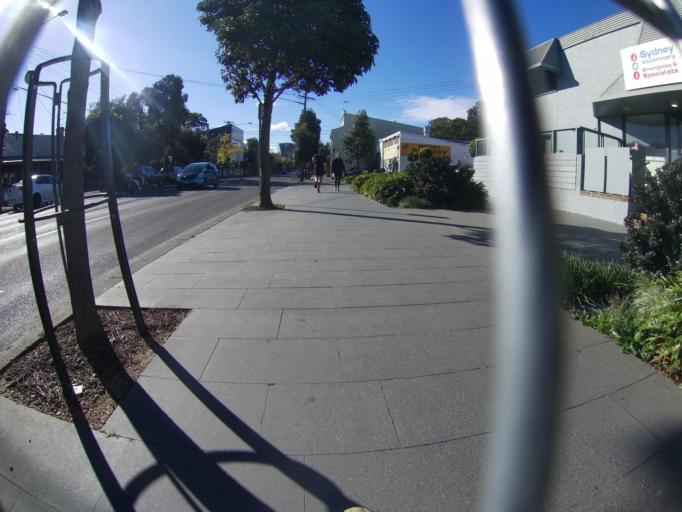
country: AU
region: New South Wales
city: Alexandria
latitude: -33.9118
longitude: 151.2019
